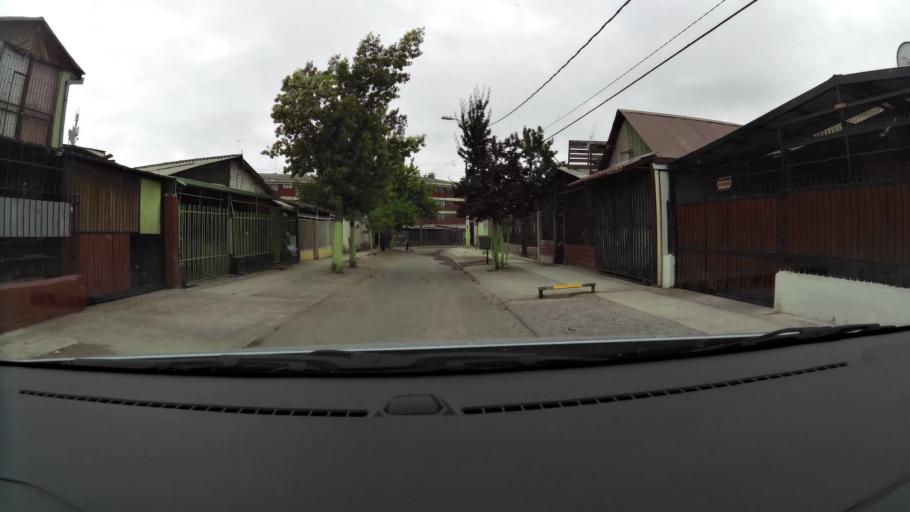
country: CL
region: Santiago Metropolitan
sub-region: Provincia de Maipo
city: San Bernardo
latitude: -33.5249
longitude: -70.6902
